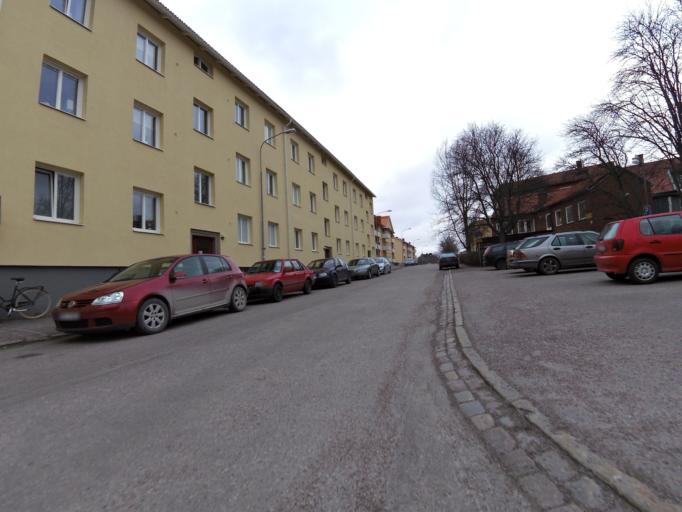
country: SE
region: Gaevleborg
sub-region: Gavle Kommun
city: Gavle
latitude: 60.6679
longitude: 17.1641
